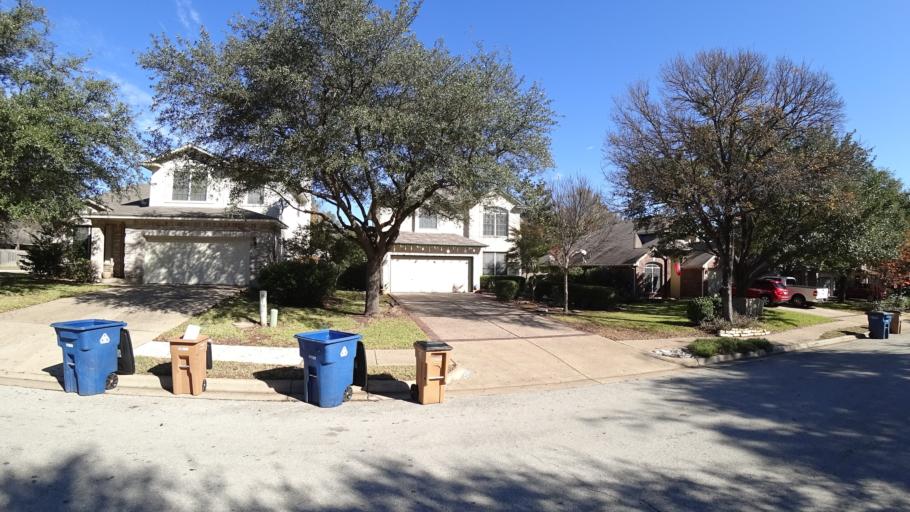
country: US
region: Texas
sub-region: Travis County
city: Wells Branch
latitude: 30.4275
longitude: -97.7176
